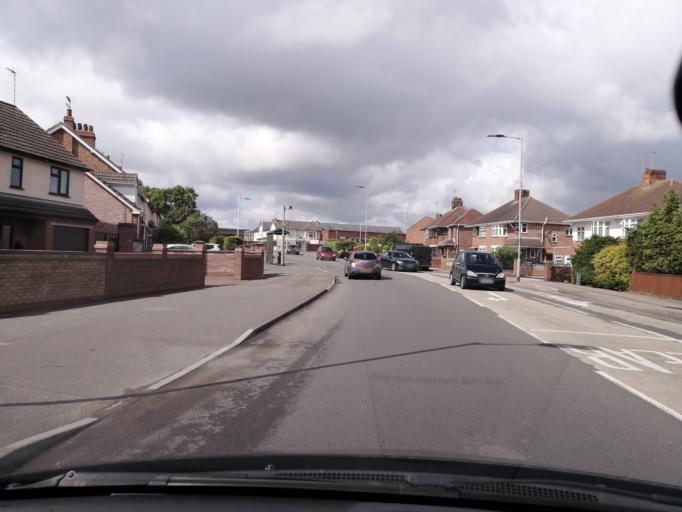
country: GB
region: England
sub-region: Peterborough
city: Peterborough
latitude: 52.5581
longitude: -0.2495
